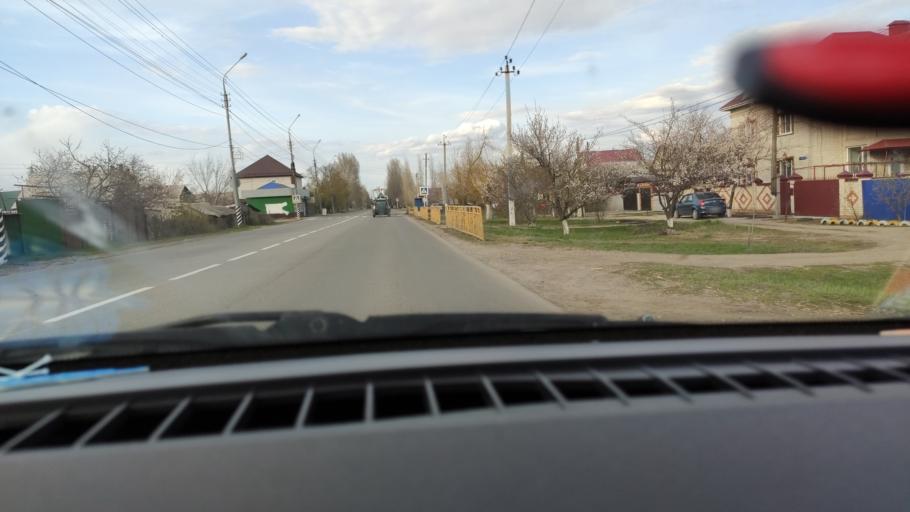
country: RU
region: Saratov
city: Privolzhskiy
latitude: 51.4335
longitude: 46.0579
